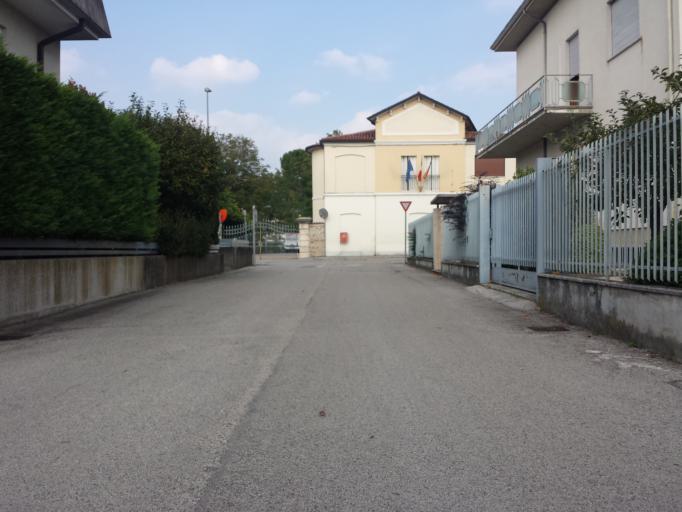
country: IT
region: Veneto
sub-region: Provincia di Vicenza
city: Sandrigo
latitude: 45.6583
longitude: 11.5995
